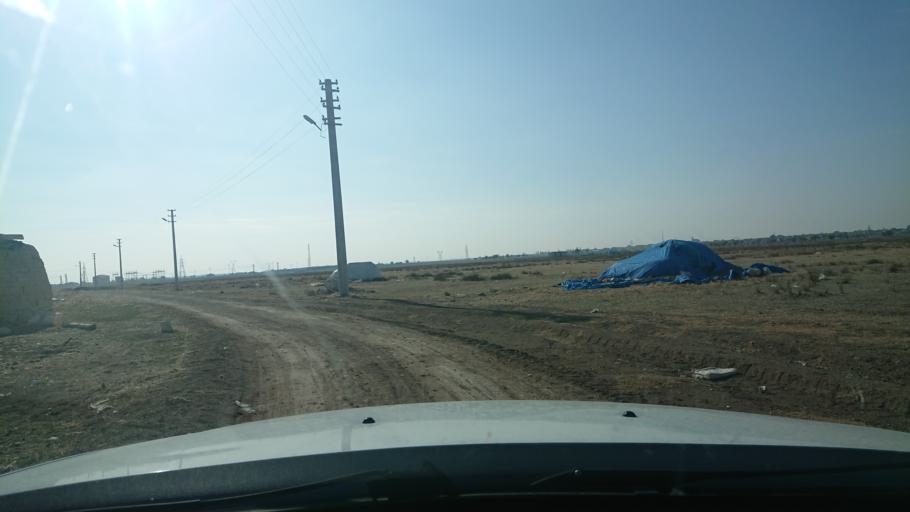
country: TR
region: Aksaray
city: Sultanhani
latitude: 38.2607
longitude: 33.4720
